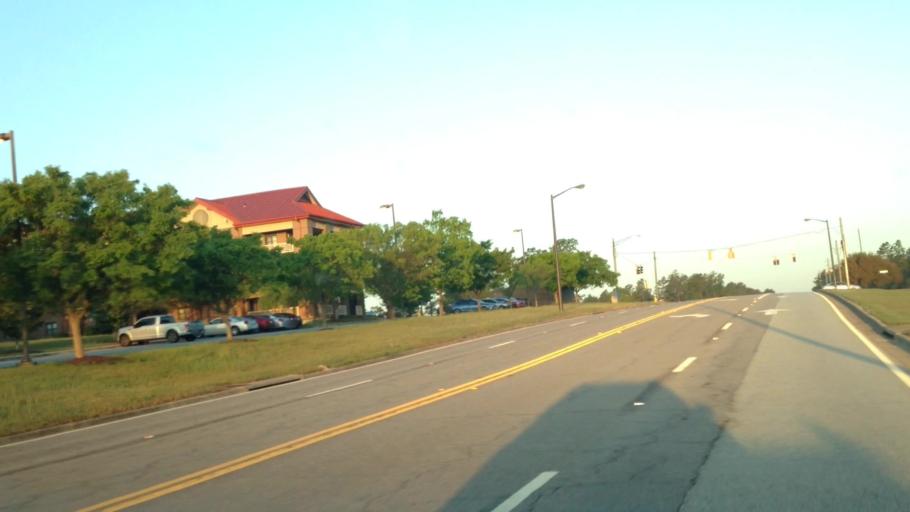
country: US
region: Georgia
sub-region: Columbia County
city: Grovetown
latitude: 33.4257
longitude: -82.1617
